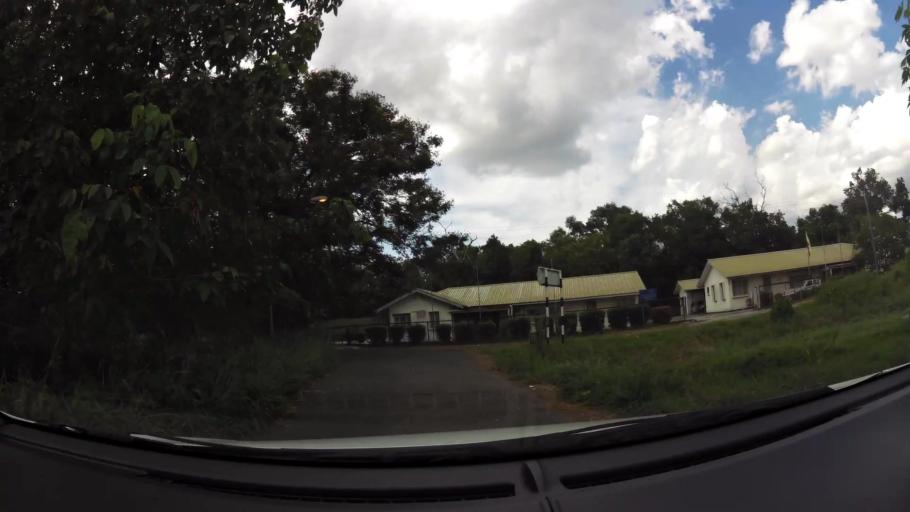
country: BN
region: Brunei and Muara
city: Bandar Seri Begawan
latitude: 4.9474
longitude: 114.9546
